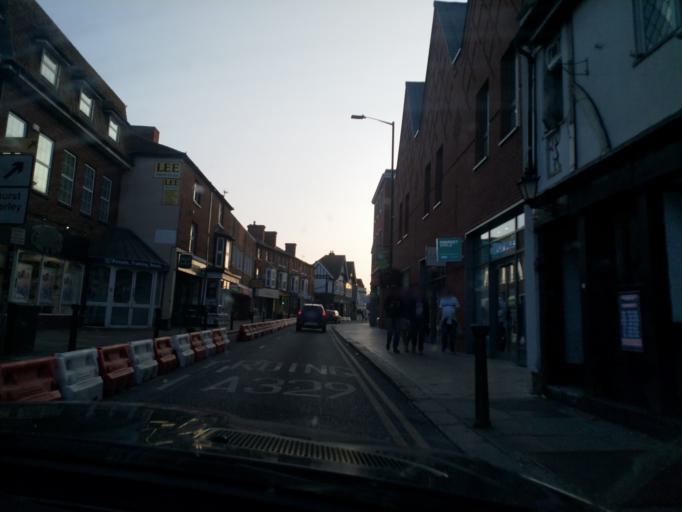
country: GB
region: England
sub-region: Kent
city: Sheerness
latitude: 51.4108
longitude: 0.8322
